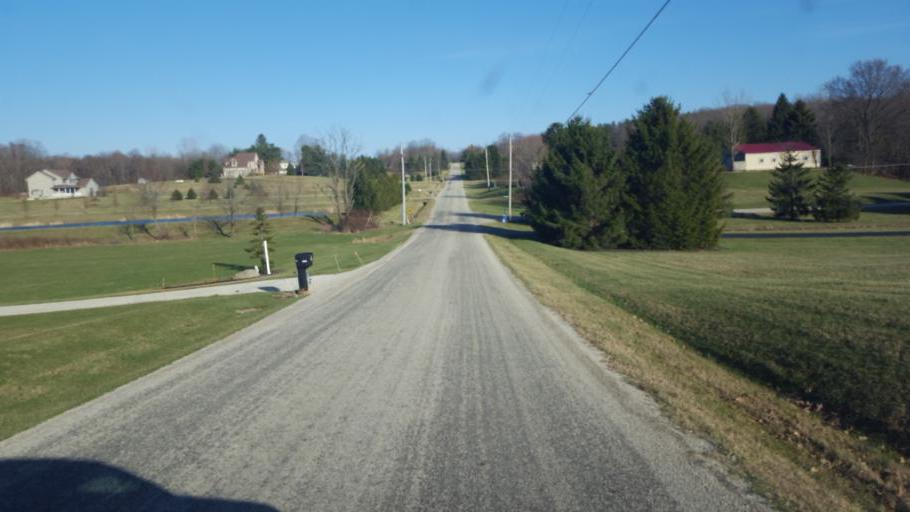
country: US
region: Ohio
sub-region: Richland County
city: Ontario
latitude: 40.7300
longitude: -82.6281
